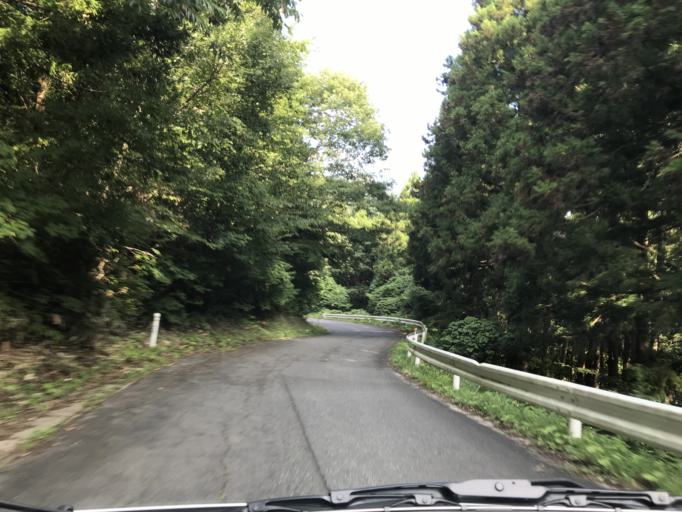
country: JP
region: Iwate
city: Ofunato
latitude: 38.9786
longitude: 141.4671
